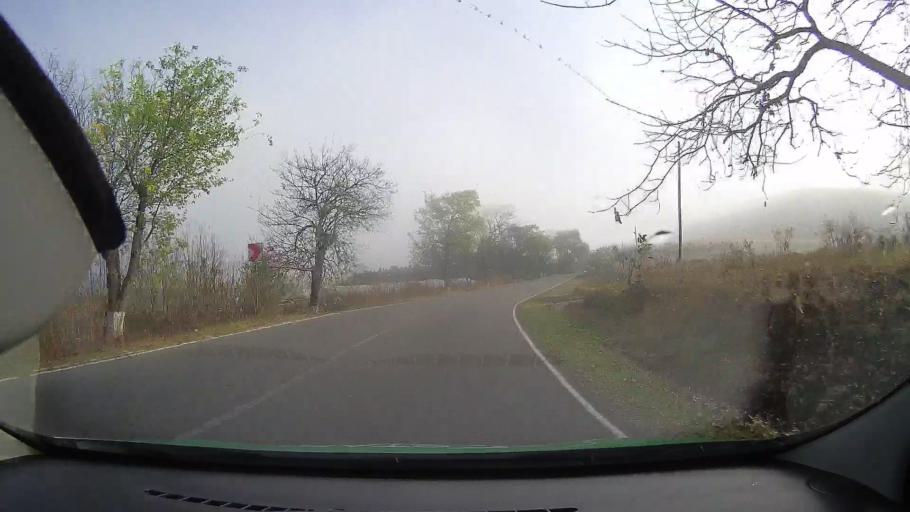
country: RO
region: Tulcea
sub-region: Comuna Nufaru
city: Nufaru
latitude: 45.1469
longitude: 28.9040
